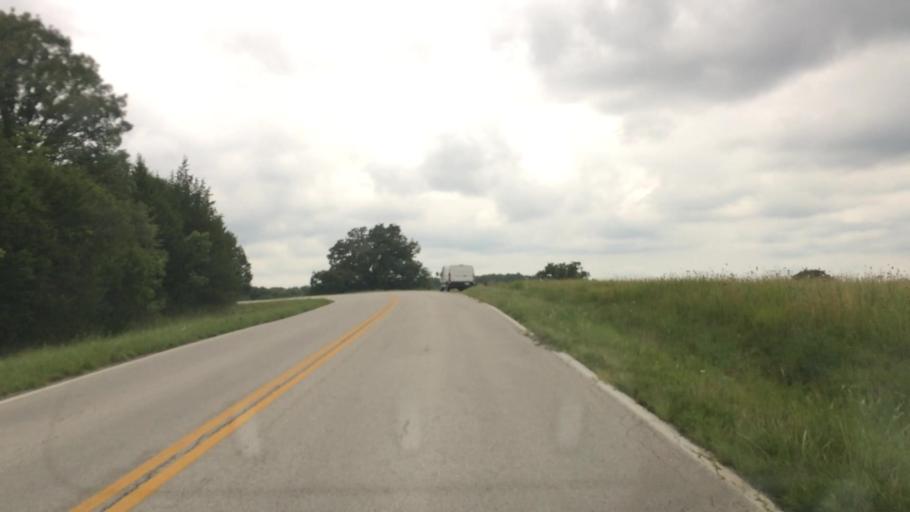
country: US
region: Missouri
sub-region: Webster County
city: Marshfield
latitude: 37.3036
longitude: -93.0053
